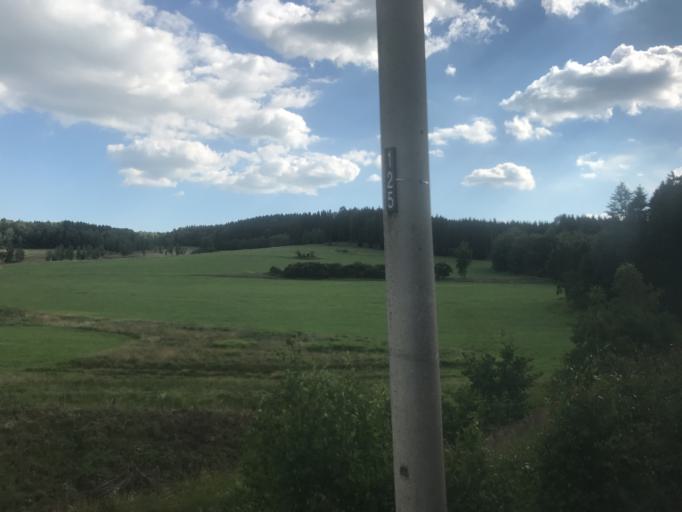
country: CZ
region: Jihocesky
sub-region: Okres Cesky Krumlov
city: Dolni Dvoriste
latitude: 48.6395
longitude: 14.4333
